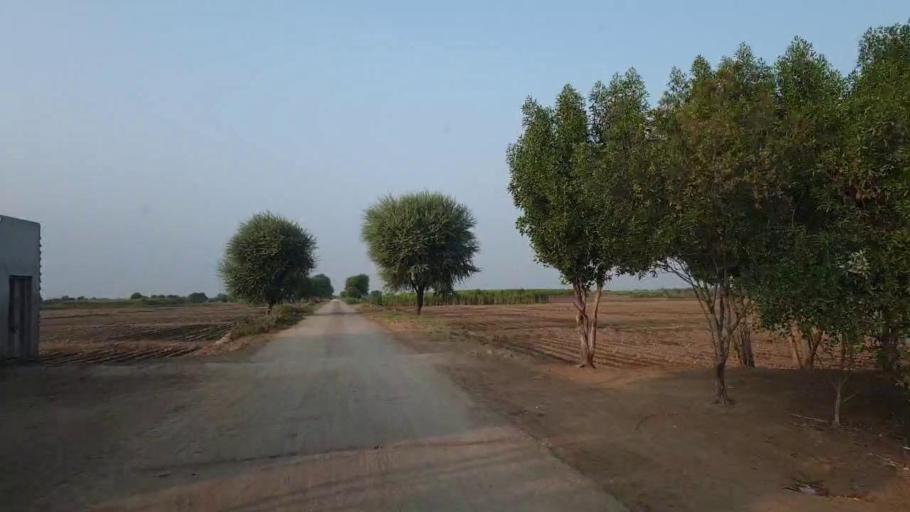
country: PK
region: Sindh
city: Tando Ghulam Ali
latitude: 25.0727
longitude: 68.9595
